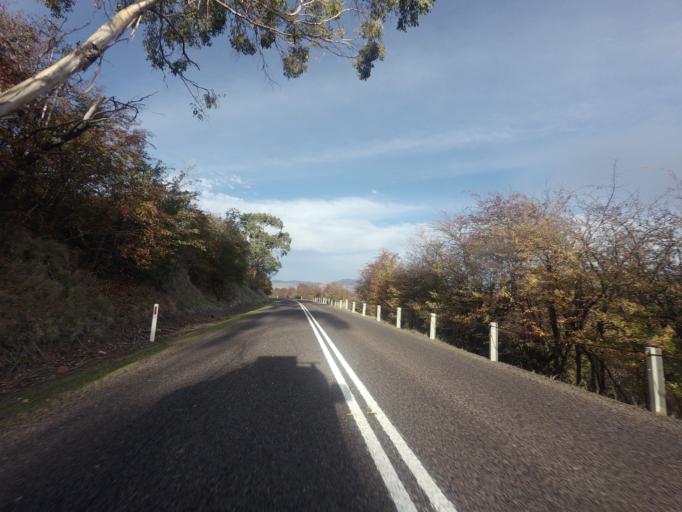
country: AU
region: Tasmania
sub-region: Brighton
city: Bridgewater
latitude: -42.4642
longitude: 147.1633
